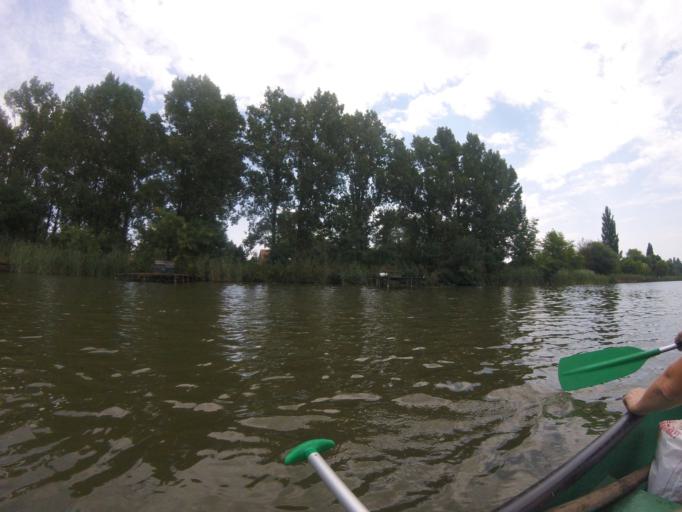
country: HU
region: Pest
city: Rackeve
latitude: 47.1769
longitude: 18.9511
